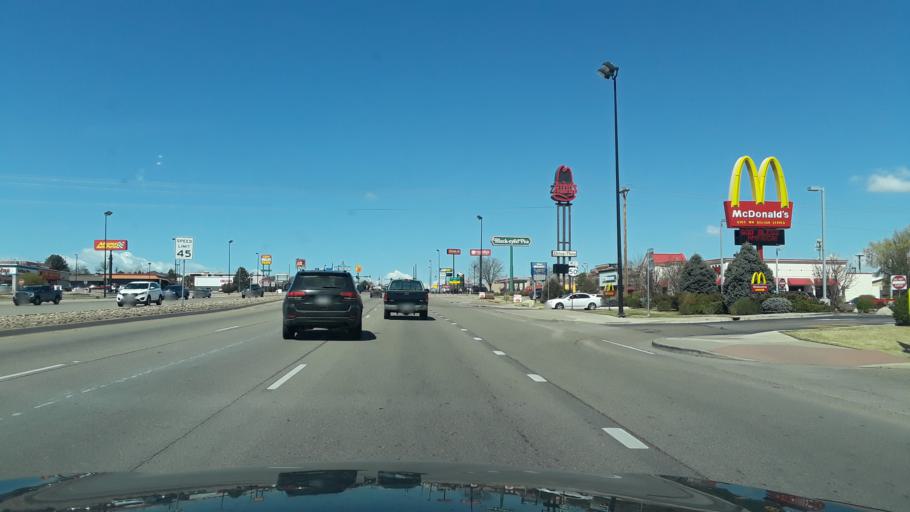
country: US
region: Colorado
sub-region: Pueblo County
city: Pueblo
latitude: 38.3079
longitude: -104.6169
